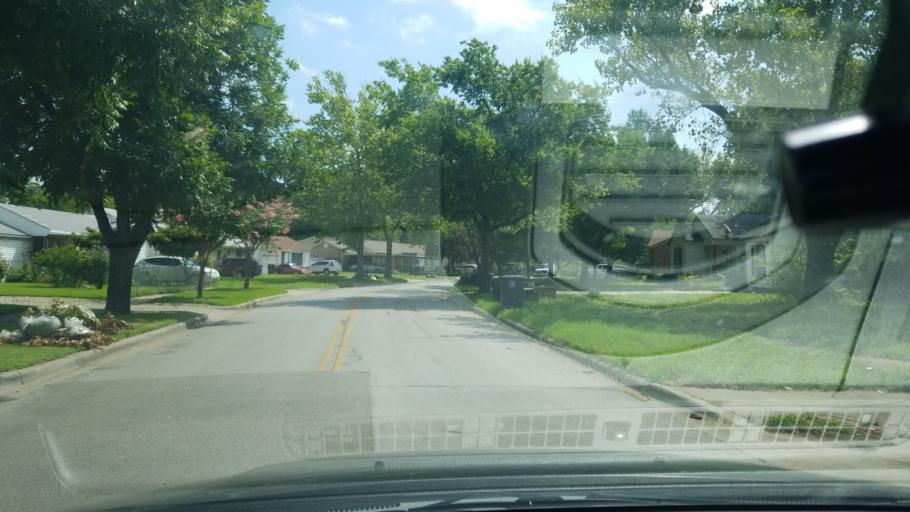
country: US
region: Texas
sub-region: Dallas County
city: Balch Springs
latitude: 32.7386
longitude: -96.6888
